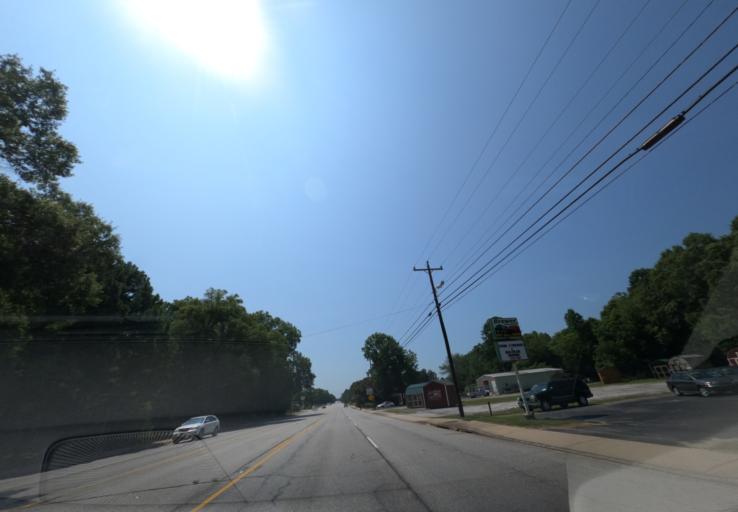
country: US
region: South Carolina
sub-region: Greenwood County
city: Greenwood
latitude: 34.1497
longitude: -82.1372
